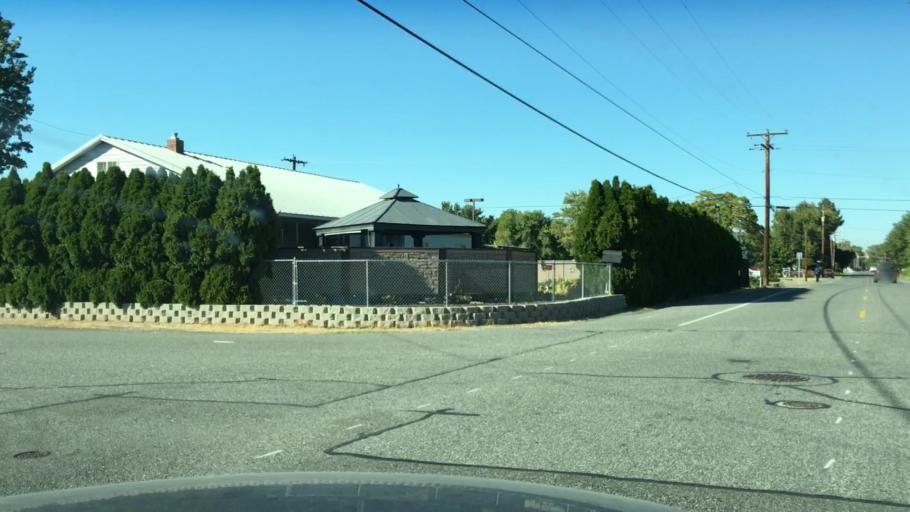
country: US
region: Washington
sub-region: Benton County
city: Kennewick
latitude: 46.2378
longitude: -119.1437
